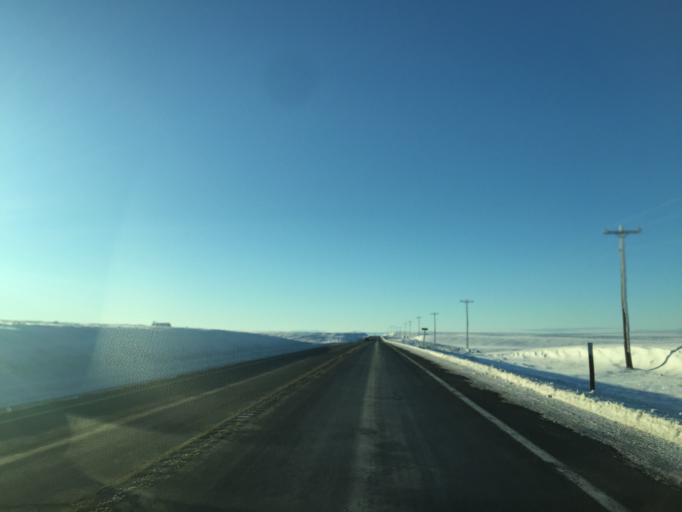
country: US
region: Washington
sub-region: Grant County
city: Soap Lake
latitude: 47.5997
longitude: -119.5275
